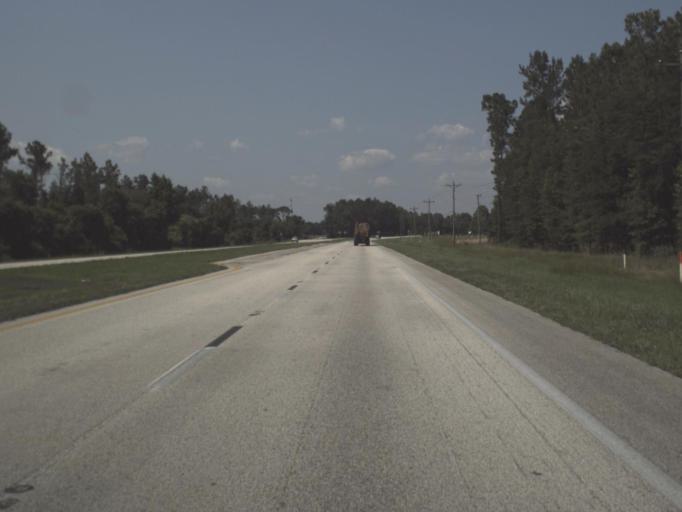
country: US
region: Florida
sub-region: Alachua County
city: Hawthorne
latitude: 29.5726
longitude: -82.0912
